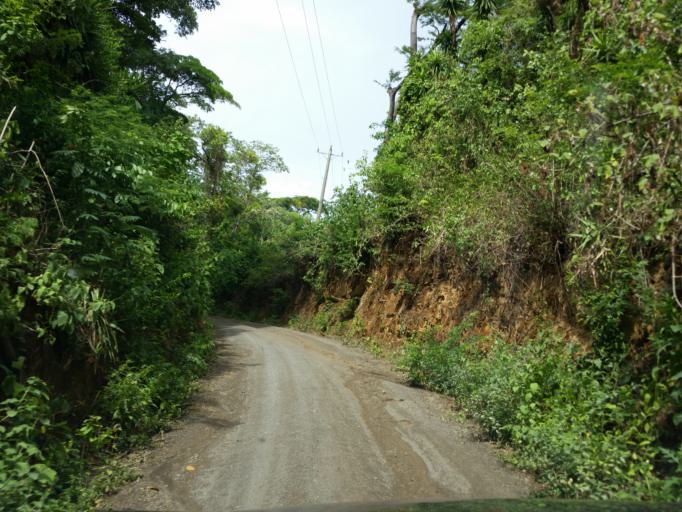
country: NI
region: Managua
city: El Crucero
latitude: 12.0087
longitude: -86.3442
